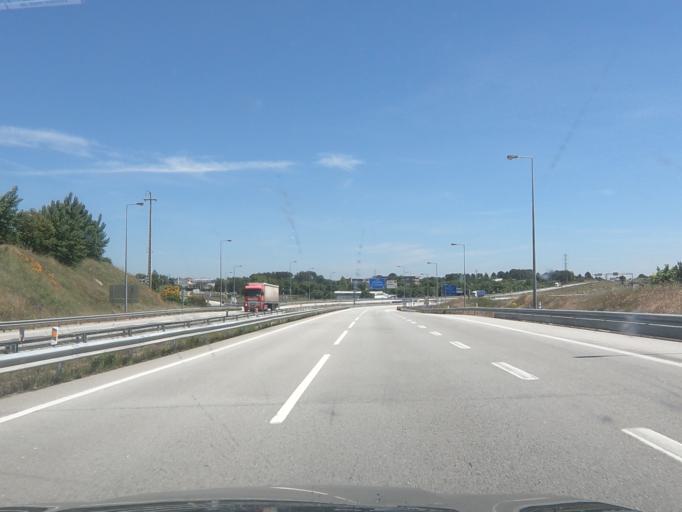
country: PT
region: Guarda
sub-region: Guarda
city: Sequeira
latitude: 40.5641
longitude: -7.2228
